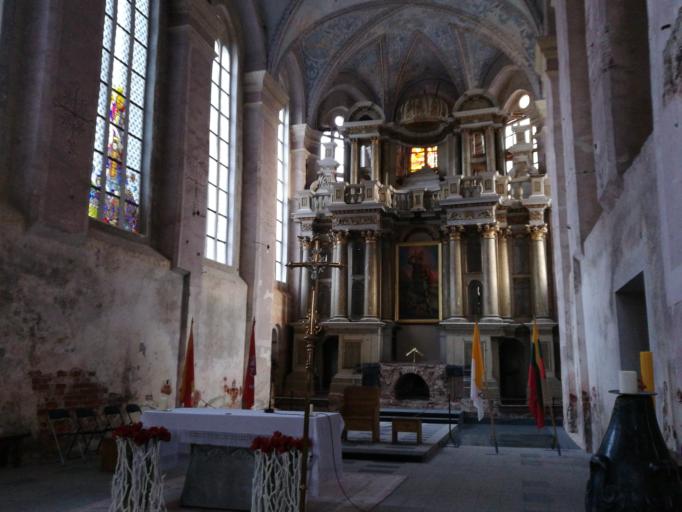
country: LT
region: Kauno apskritis
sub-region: Kaunas
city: Kaunas
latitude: 54.8981
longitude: 23.8832
